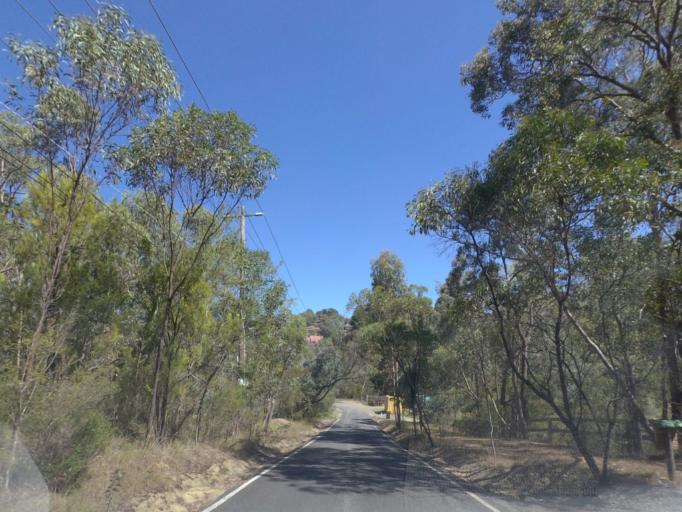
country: AU
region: Victoria
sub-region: Manningham
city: Park Orchards
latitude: -37.7941
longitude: 145.2167
